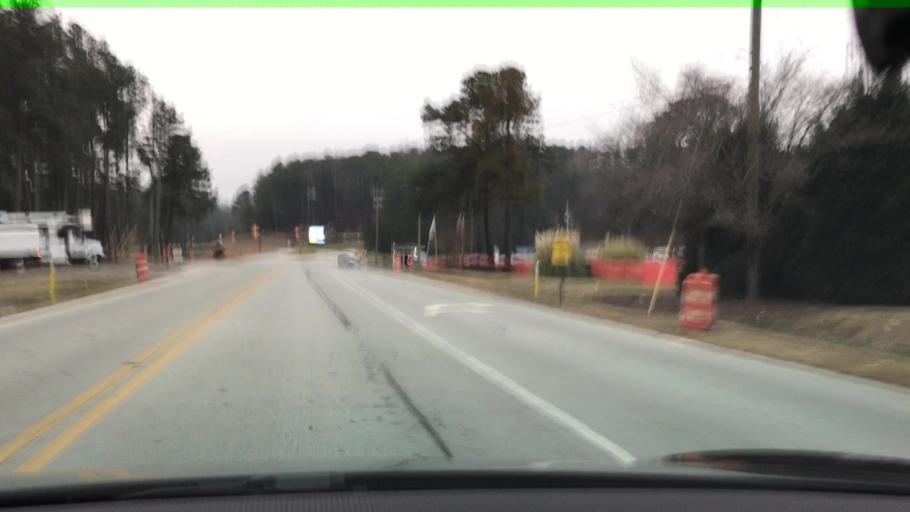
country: US
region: Georgia
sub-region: Gwinnett County
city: Buford
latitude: 34.1685
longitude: -84.0041
